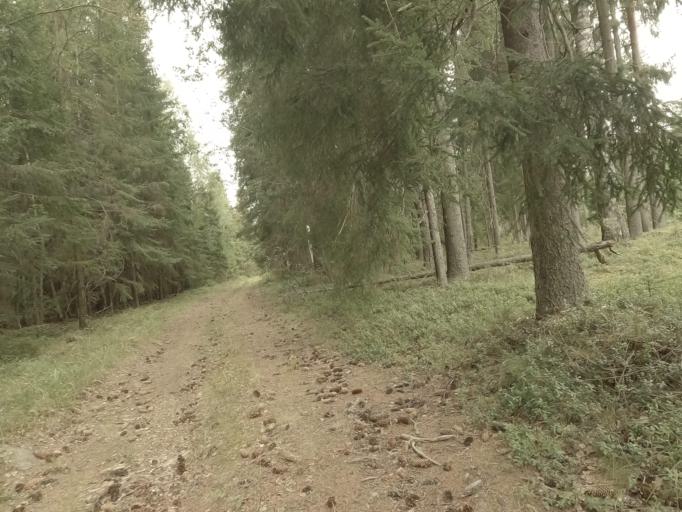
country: RU
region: Leningrad
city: Kamennogorsk
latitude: 61.0453
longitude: 29.1865
